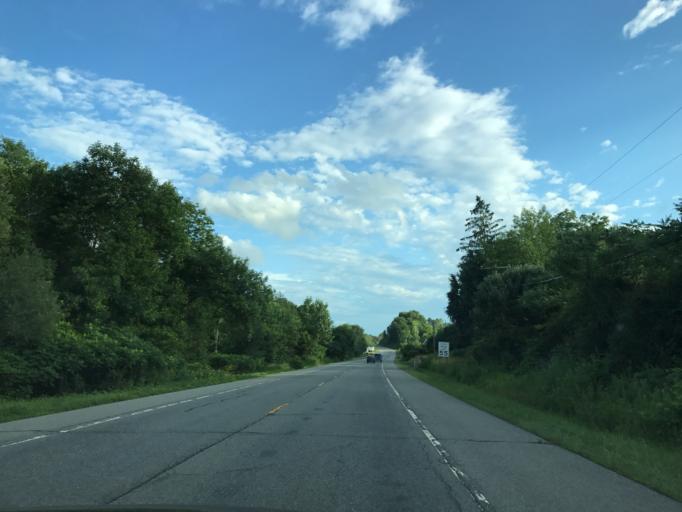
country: US
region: New York
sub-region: Saratoga County
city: Schuylerville
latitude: 43.0755
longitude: -73.5843
